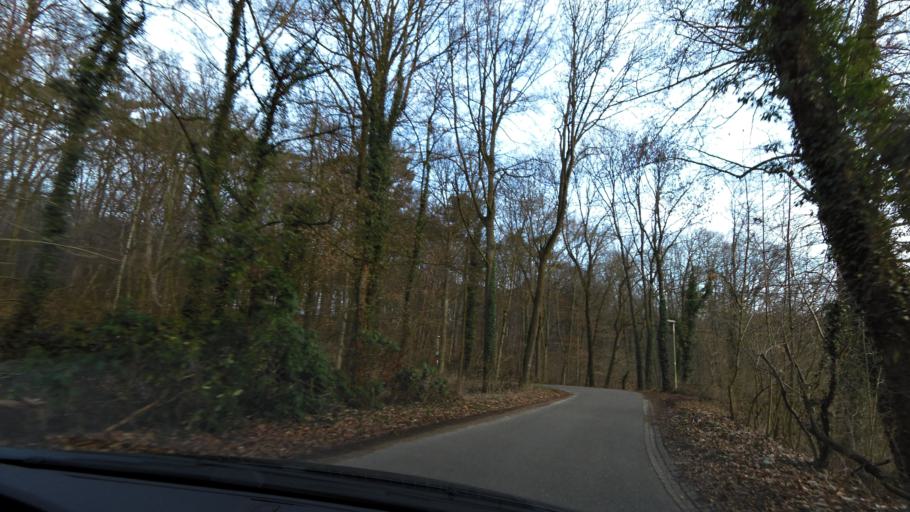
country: NL
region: Limburg
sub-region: Gemeente Schinnen
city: Puth
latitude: 50.9463
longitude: 5.8507
